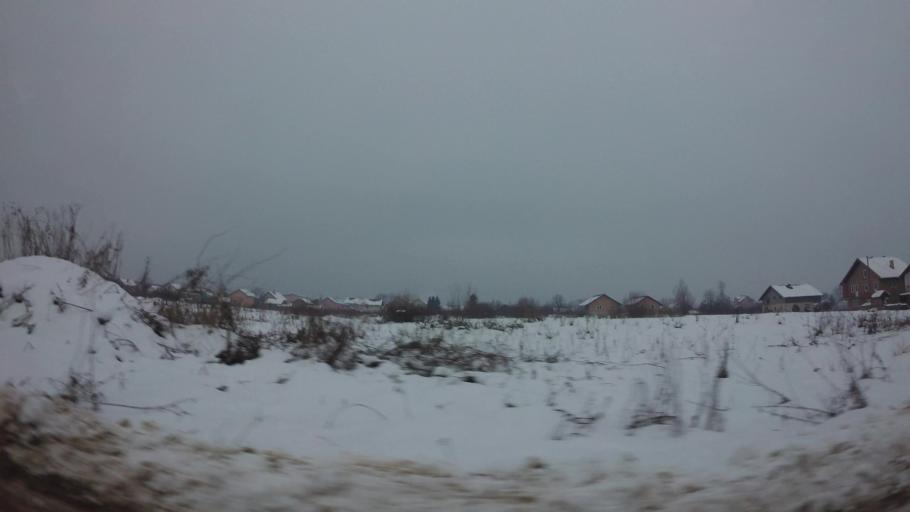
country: BA
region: Federation of Bosnia and Herzegovina
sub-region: Kanton Sarajevo
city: Sarajevo
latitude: 43.8435
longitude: 18.3092
